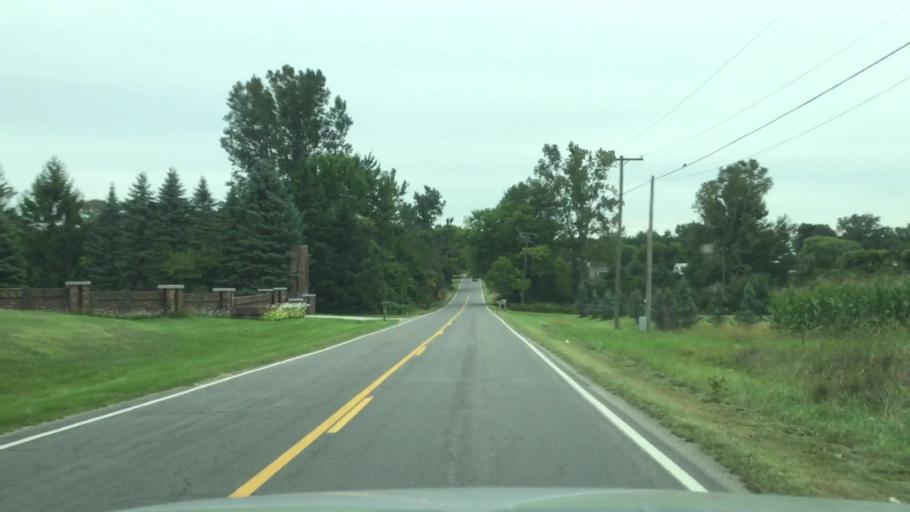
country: US
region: Michigan
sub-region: Washtenaw County
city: Milan
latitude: 42.1522
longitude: -83.6533
